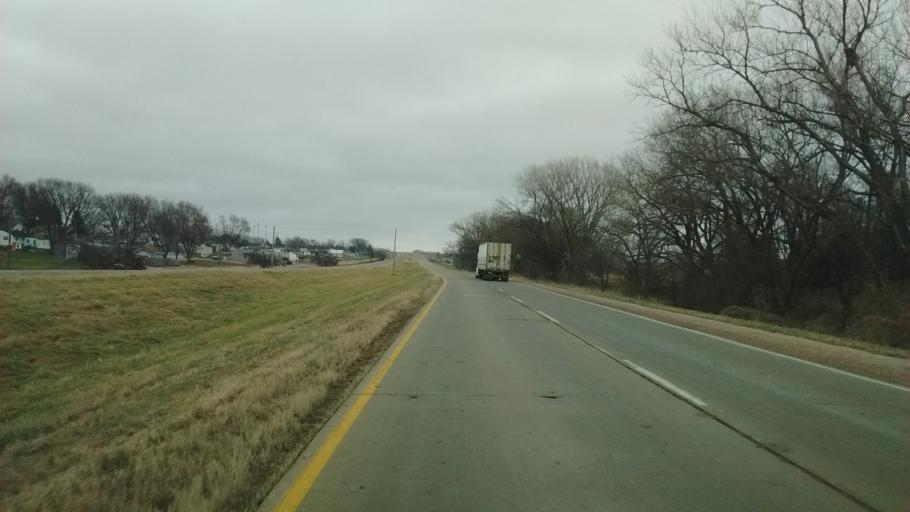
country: US
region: Iowa
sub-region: Woodbury County
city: Moville
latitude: 42.4817
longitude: -96.0725
